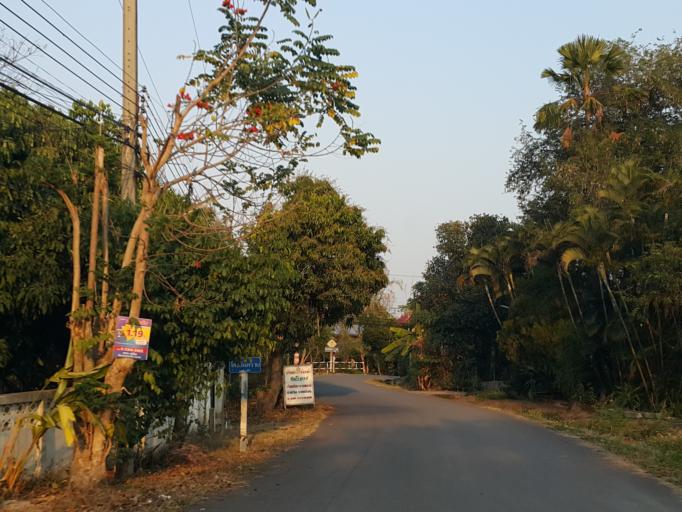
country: TH
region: Chiang Mai
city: San Sai
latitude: 18.9032
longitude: 98.9524
